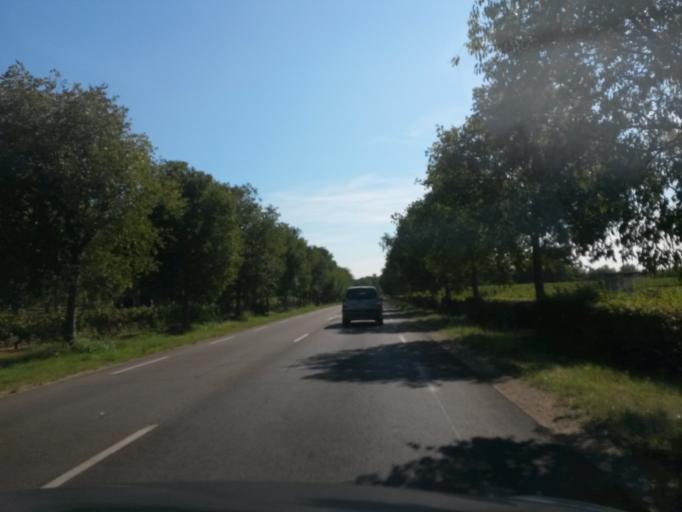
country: FR
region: Languedoc-Roussillon
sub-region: Departement de l'Herault
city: Gignac
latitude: 43.6672
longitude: 3.5672
